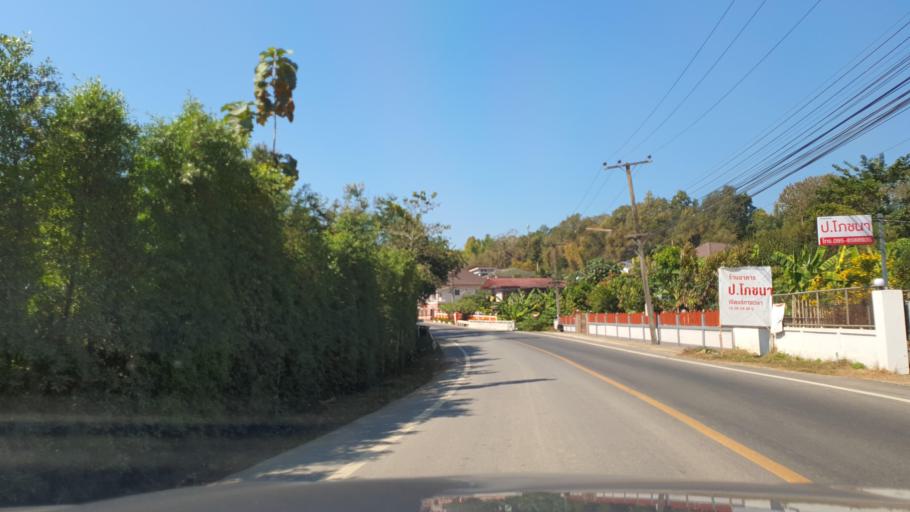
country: TH
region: Nan
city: Tha Wang Pha
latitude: 19.0814
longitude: 100.8841
